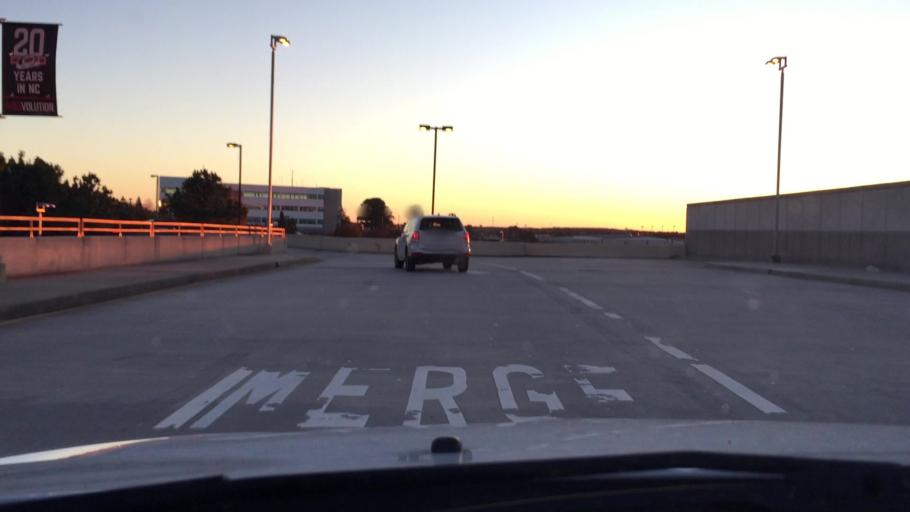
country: US
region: North Carolina
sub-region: Wake County
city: Morrisville
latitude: 35.8759
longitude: -78.7934
